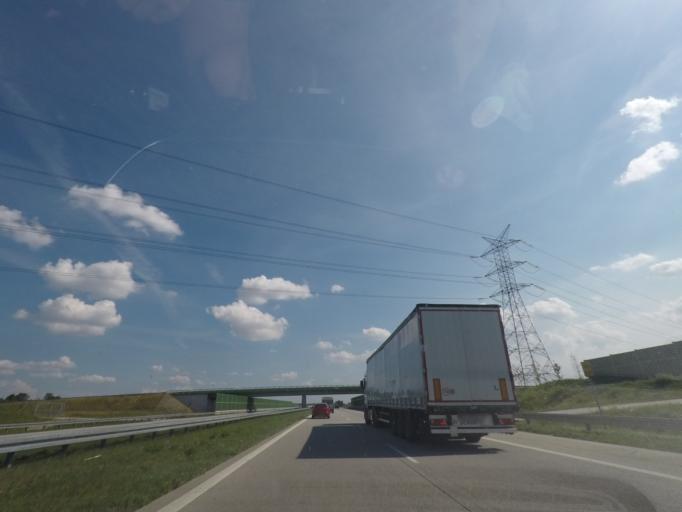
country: PL
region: Lodz Voivodeship
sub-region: Powiat lodzki wschodni
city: Tuszyn
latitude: 51.6026
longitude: 19.5786
